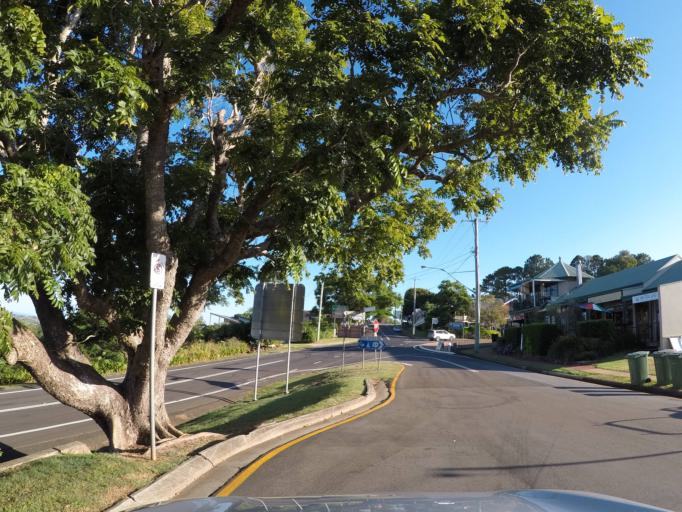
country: AU
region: Queensland
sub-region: Sunshine Coast
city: Nambour
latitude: -26.6234
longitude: 152.8662
